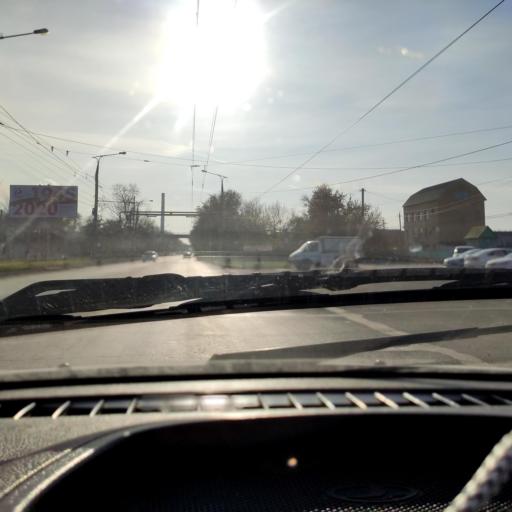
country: RU
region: Samara
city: Tol'yatti
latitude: 53.5613
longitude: 49.4544
